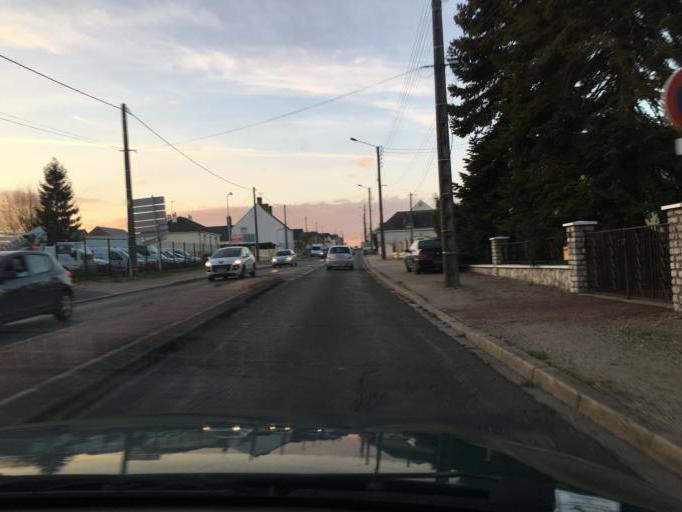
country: FR
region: Centre
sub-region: Departement du Loiret
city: Ingre
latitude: 47.9258
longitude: 1.8453
